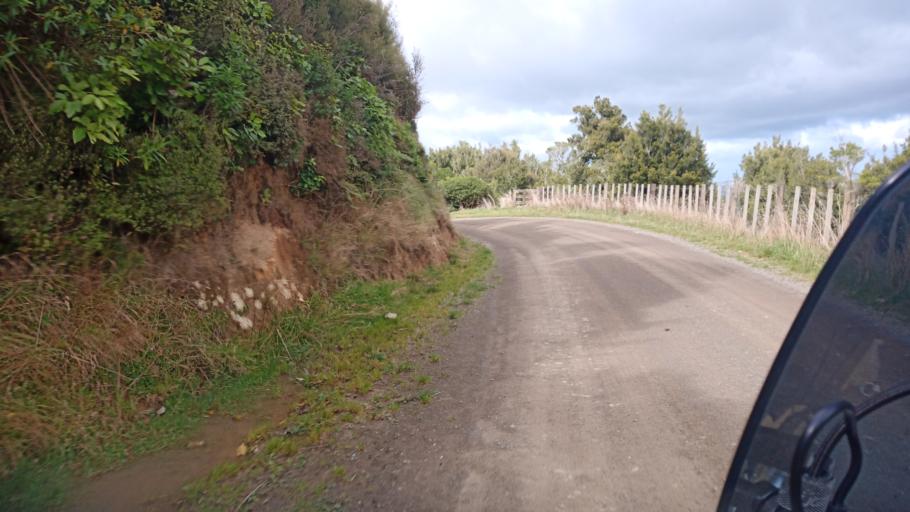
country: NZ
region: Gisborne
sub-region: Gisborne District
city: Gisborne
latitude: -38.4849
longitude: 177.6008
